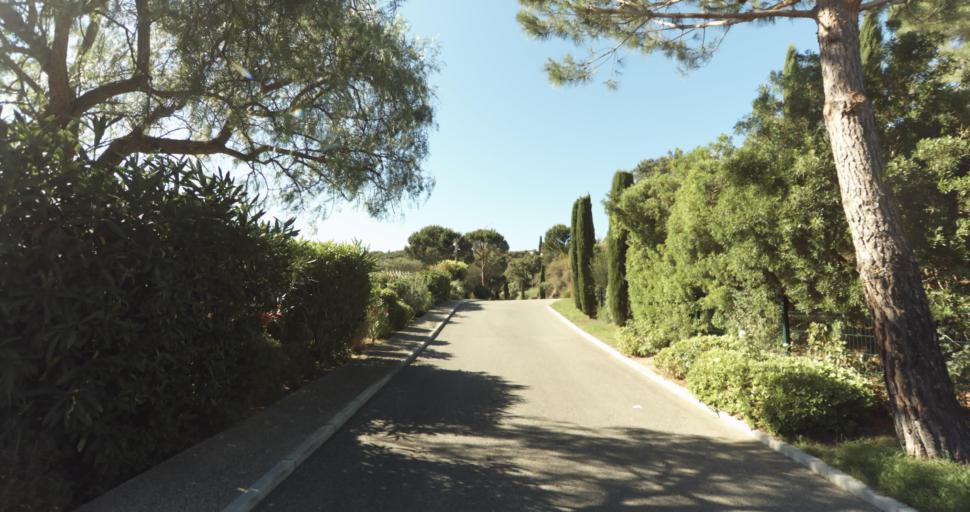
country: FR
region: Provence-Alpes-Cote d'Azur
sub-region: Departement du Var
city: Gassin
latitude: 43.2558
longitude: 6.6071
